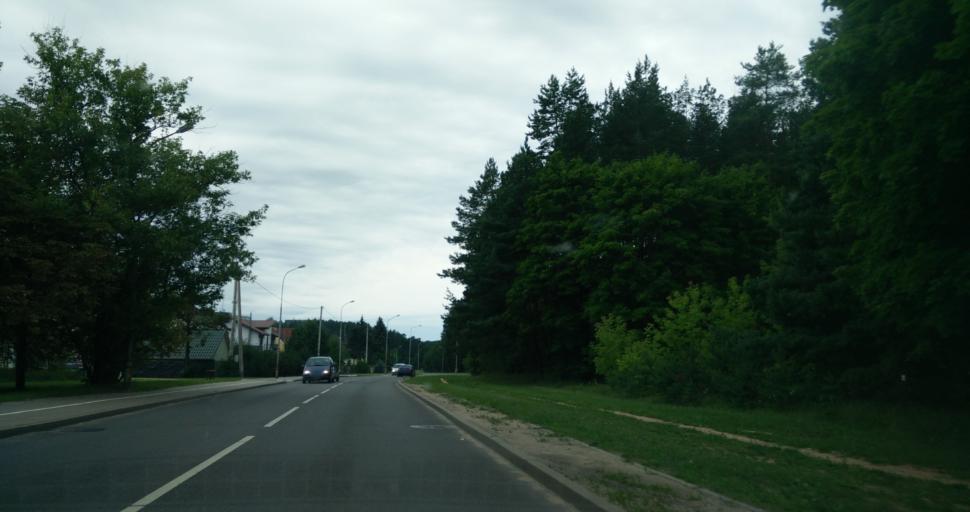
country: LT
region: Vilnius County
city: Rasos
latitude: 54.7274
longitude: 25.3461
